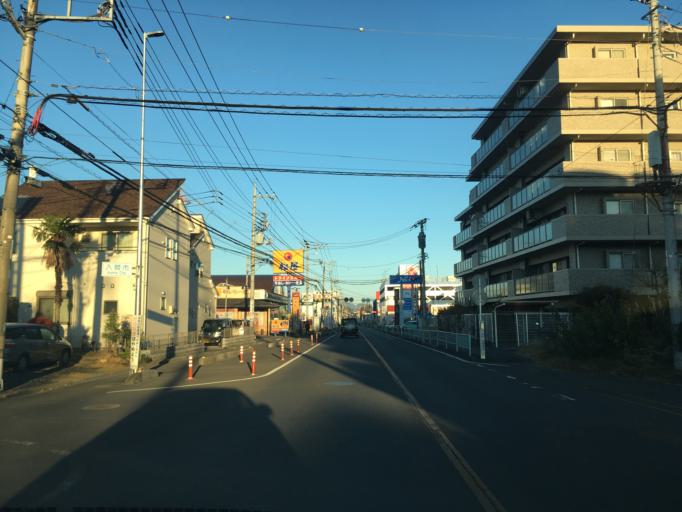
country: JP
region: Saitama
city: Sayama
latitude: 35.8178
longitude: 139.4190
